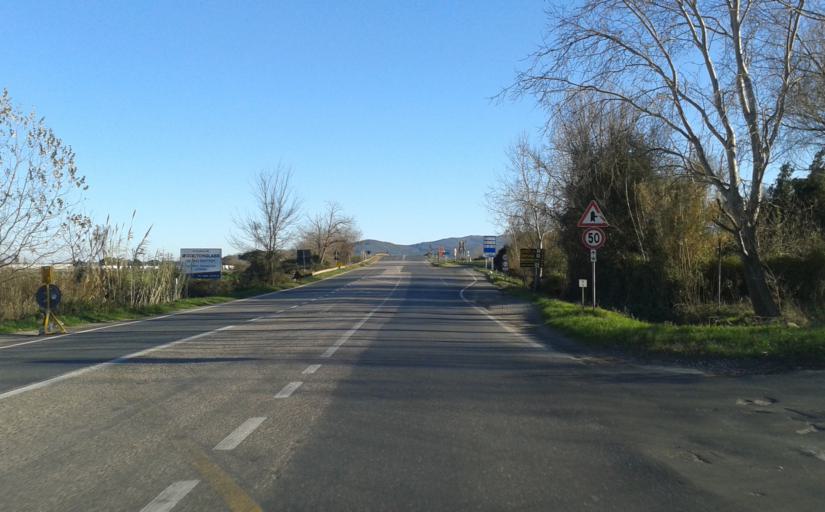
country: IT
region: Tuscany
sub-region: Provincia di Livorno
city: Livorno
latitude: 43.5754
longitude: 10.3436
